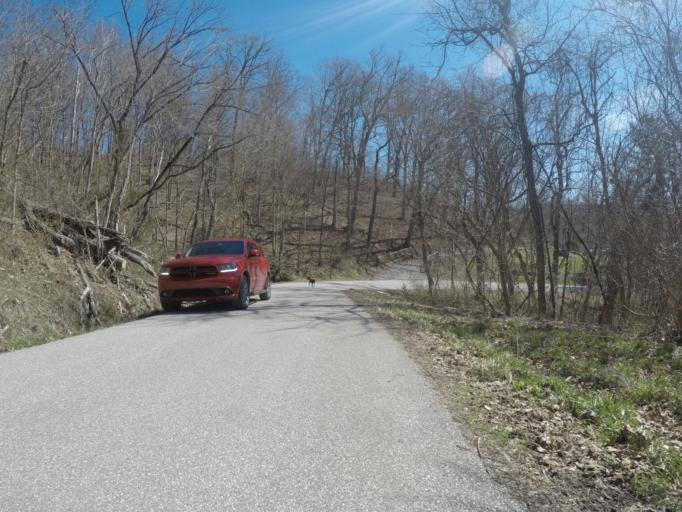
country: US
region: Ohio
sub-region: Lawrence County
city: South Point
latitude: 38.4806
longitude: -82.5659
